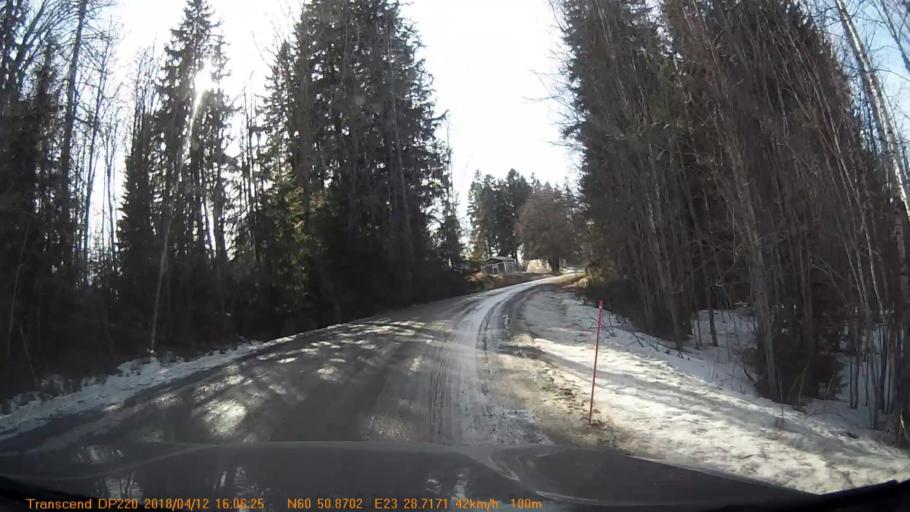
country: FI
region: Haeme
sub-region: Forssa
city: Jokioinen
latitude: 60.8478
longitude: 23.4784
